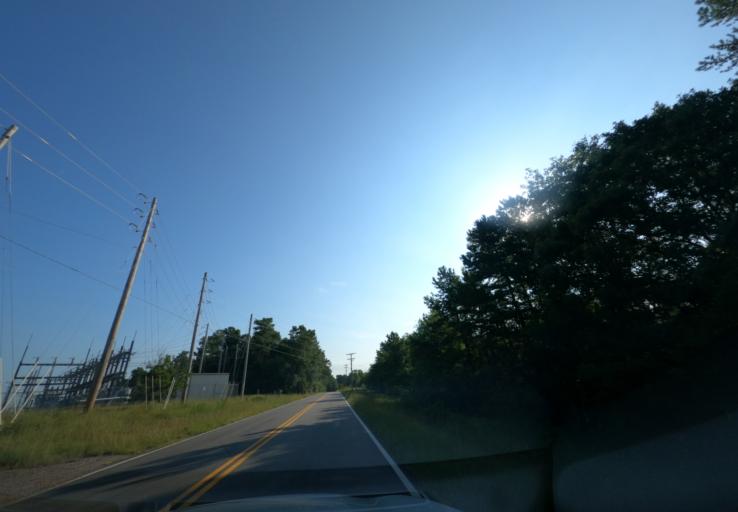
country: US
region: South Carolina
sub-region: Edgefield County
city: Murphys Estates
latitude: 33.5806
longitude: -81.9891
